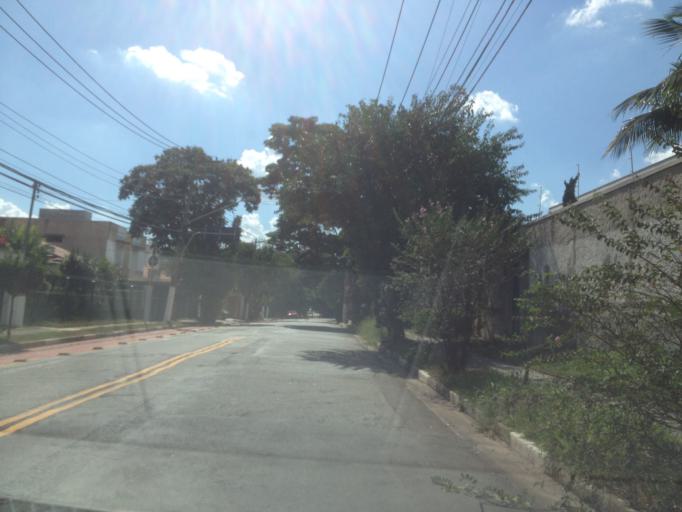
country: BR
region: Sao Paulo
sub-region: Osasco
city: Osasco
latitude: -23.5262
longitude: -46.7209
